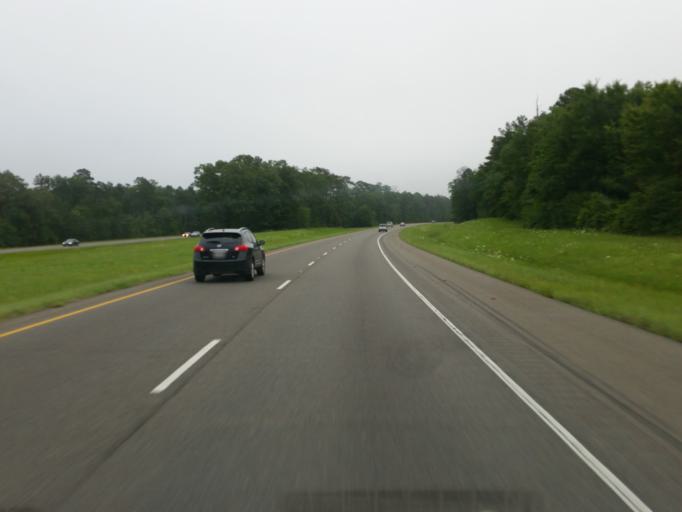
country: US
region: Louisiana
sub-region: Bossier Parish
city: Haughton
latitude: 32.5740
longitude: -93.4815
